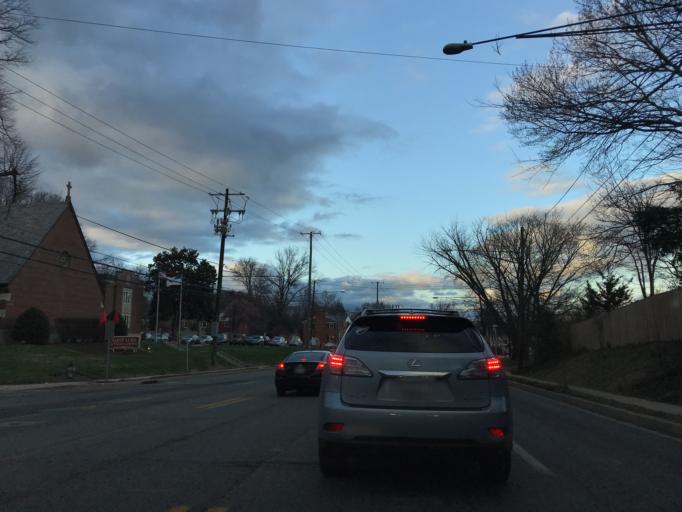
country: US
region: Maryland
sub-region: Montgomery County
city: Silver Spring
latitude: 39.0043
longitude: -77.0235
